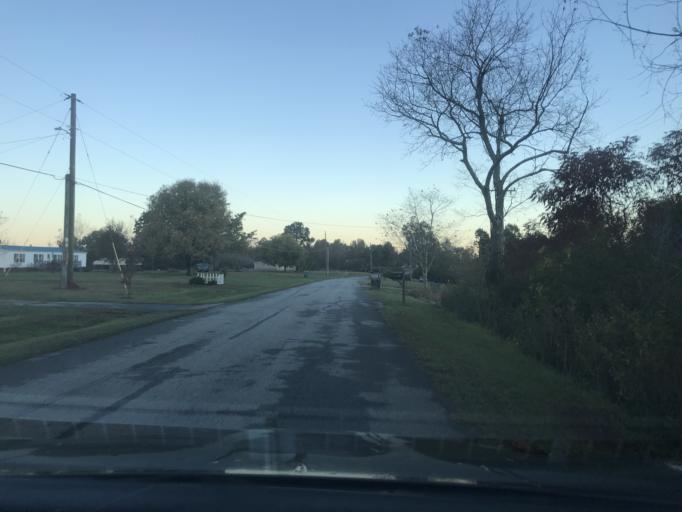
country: US
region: South Carolina
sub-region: Spartanburg County
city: Mayo
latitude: 35.1207
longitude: -81.7749
